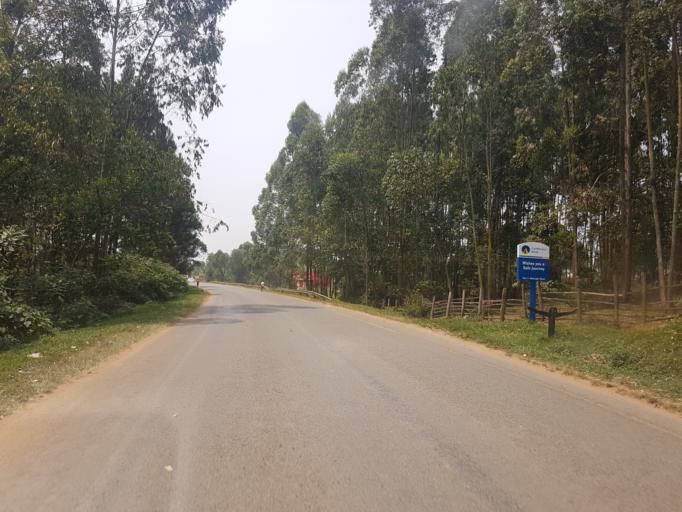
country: UG
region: Western Region
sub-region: Bushenyi District
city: Bushenyi
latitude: -0.5413
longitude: 30.1557
